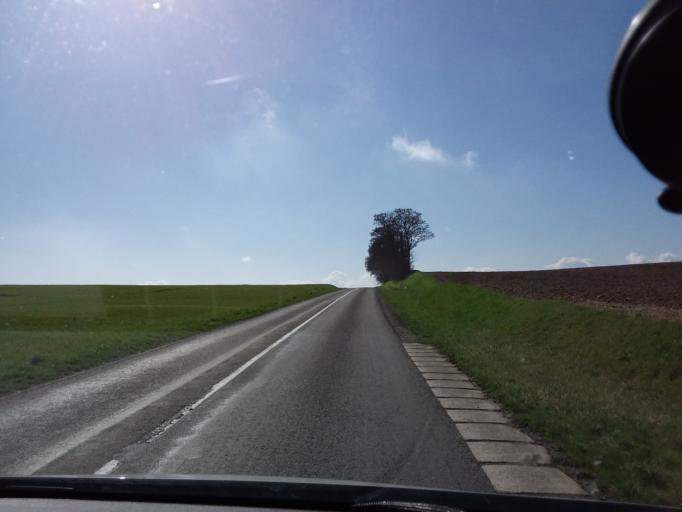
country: FR
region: Picardie
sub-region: Departement de l'Aisne
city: Guignicourt
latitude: 49.5086
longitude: 4.0407
